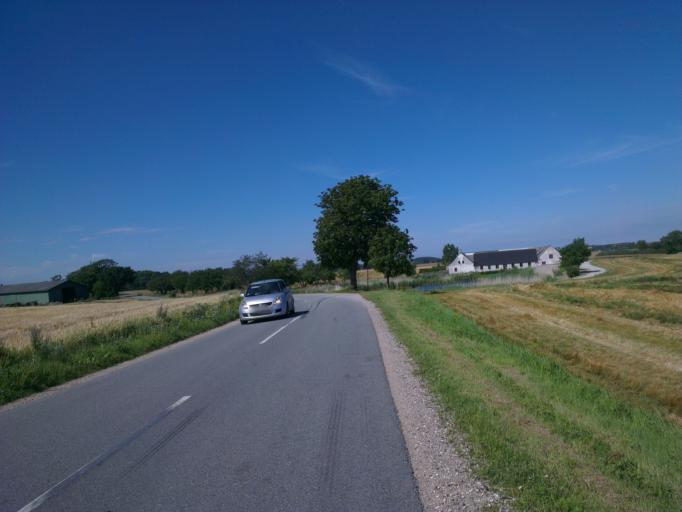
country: DK
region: Capital Region
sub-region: Frederikssund Kommune
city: Slangerup
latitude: 55.8580
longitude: 12.1551
